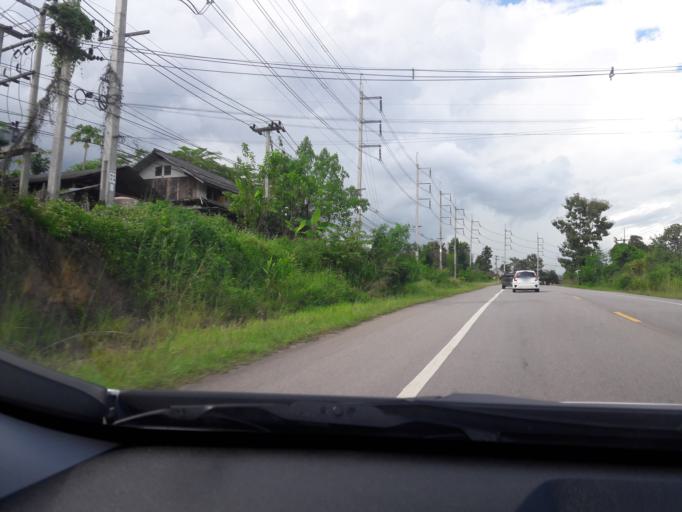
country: TH
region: Mae Hong Son
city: Mae Hi
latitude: 19.3330
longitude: 98.4326
